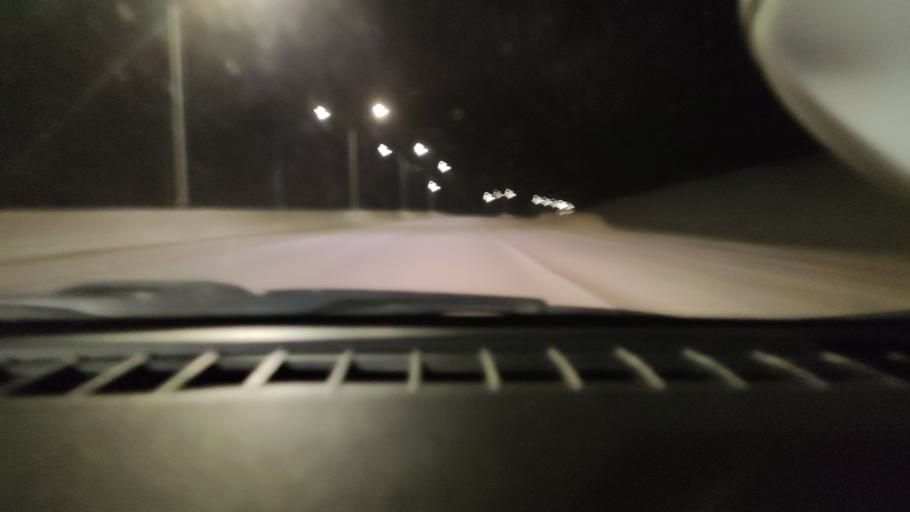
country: RU
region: Perm
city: Novyye Lyady
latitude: 58.0617
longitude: 56.4272
